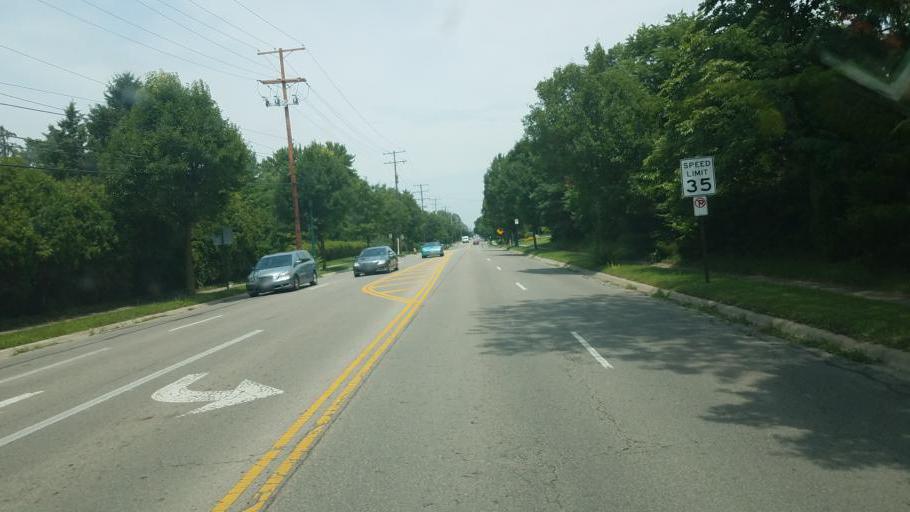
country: US
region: Ohio
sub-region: Franklin County
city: Upper Arlington
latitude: 40.0410
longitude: -83.0667
